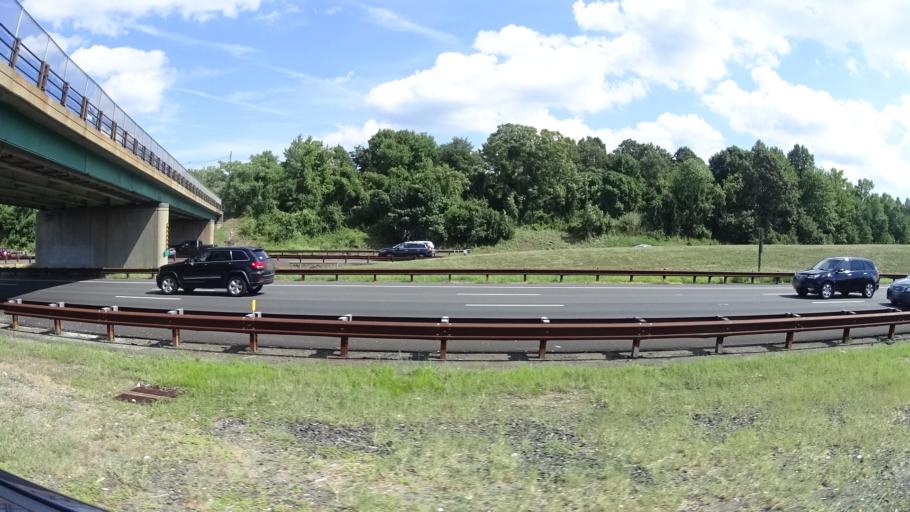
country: US
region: New Jersey
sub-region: Monmouth County
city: Keyport
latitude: 40.4208
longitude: -74.2125
